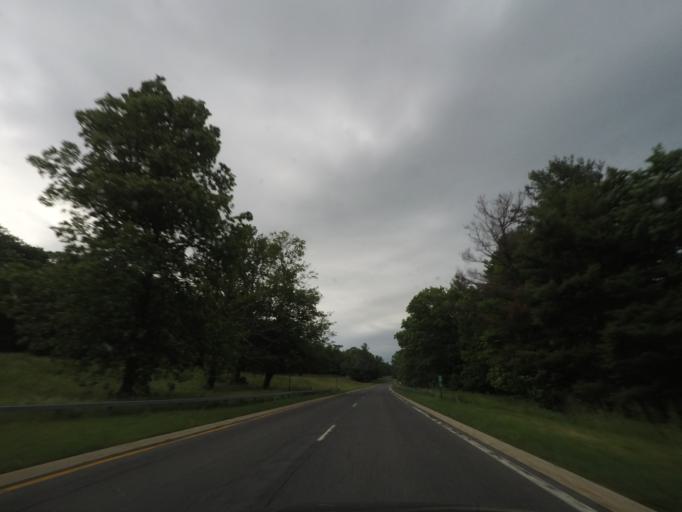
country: US
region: New York
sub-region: Columbia County
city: Chatham
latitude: 42.2983
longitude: -73.5823
